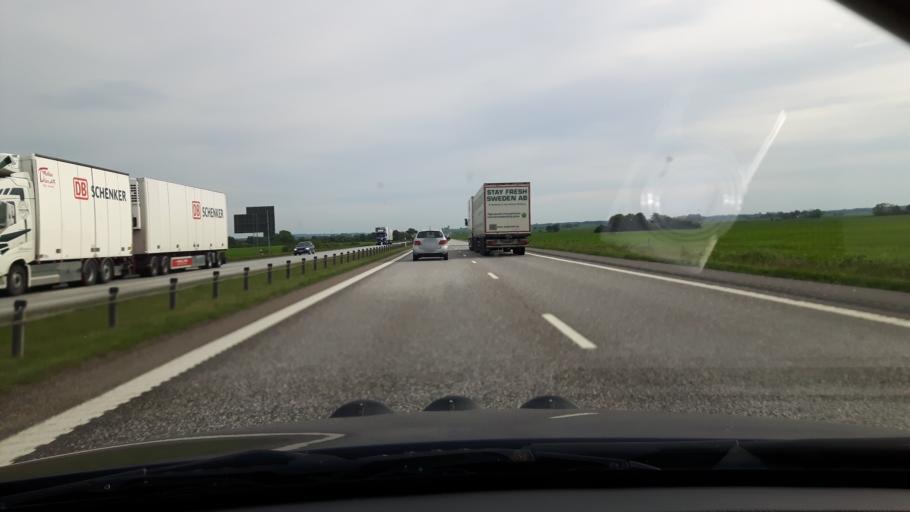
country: SE
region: Skane
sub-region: Angelholms Kommun
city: AEngelholm
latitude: 56.3078
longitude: 12.9091
